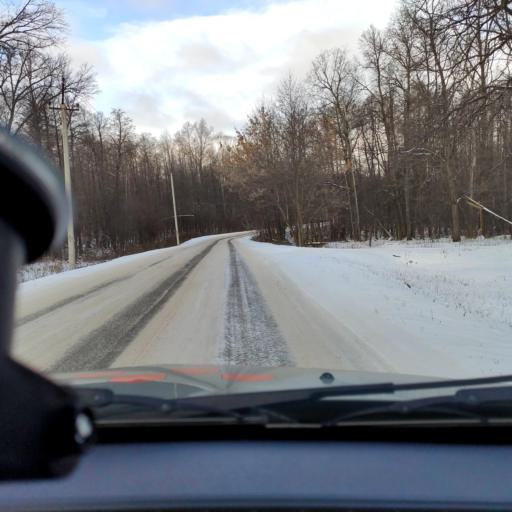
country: RU
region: Bashkortostan
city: Avdon
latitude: 54.7804
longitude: 55.7517
